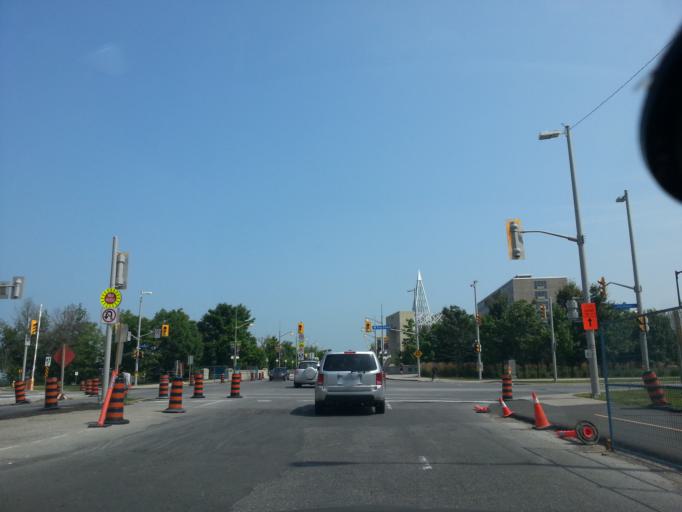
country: CA
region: Ontario
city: Ottawa
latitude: 45.4382
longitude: -75.6966
